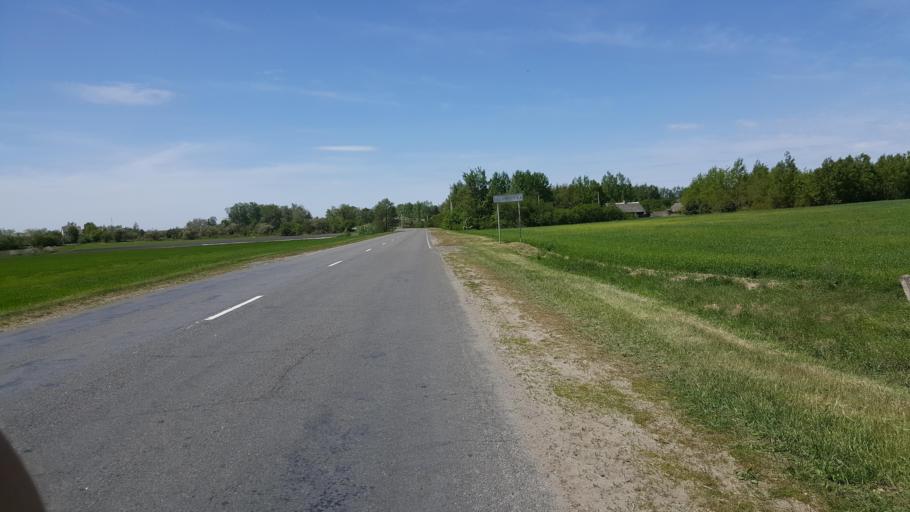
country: BY
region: Brest
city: Kobryn
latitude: 52.3508
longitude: 24.1933
